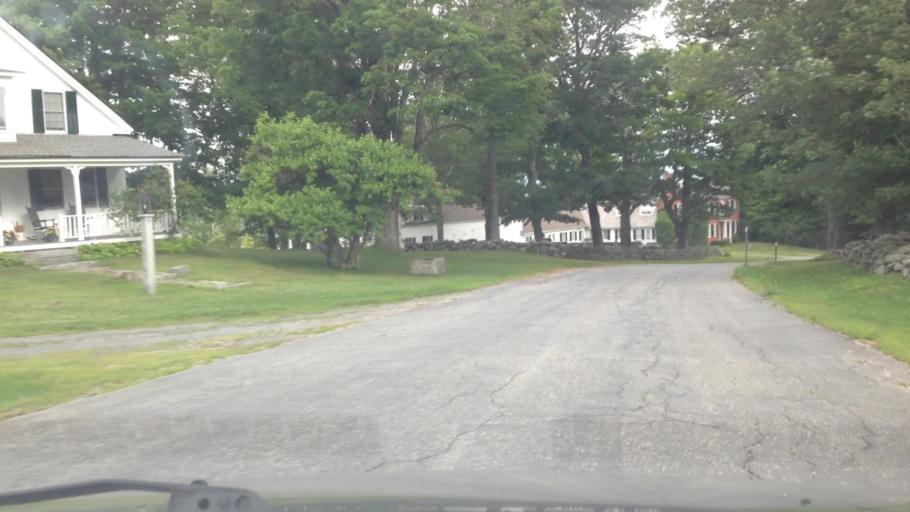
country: US
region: New Hampshire
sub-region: Cheshire County
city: Marlborough
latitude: 42.8936
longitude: -72.1949
